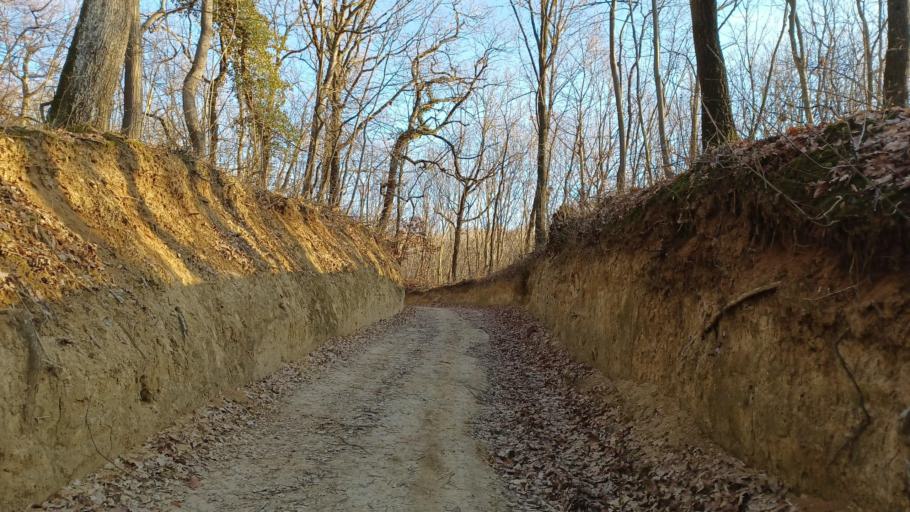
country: HU
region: Tolna
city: Szentgalpuszta
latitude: 46.3208
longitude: 18.6282
